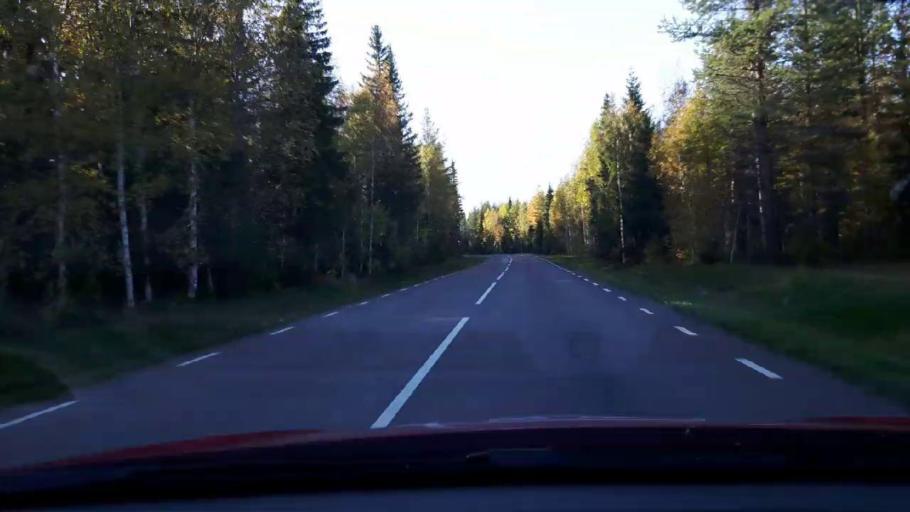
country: SE
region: Jaemtland
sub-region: Stroemsunds Kommun
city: Stroemsund
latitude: 63.8432
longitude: 15.4248
